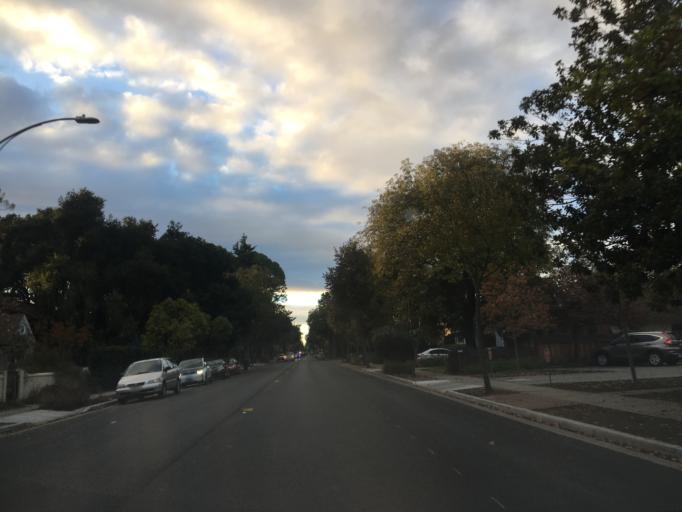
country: US
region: California
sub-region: Santa Clara County
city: Palo Alto
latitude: 37.4446
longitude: -122.1471
